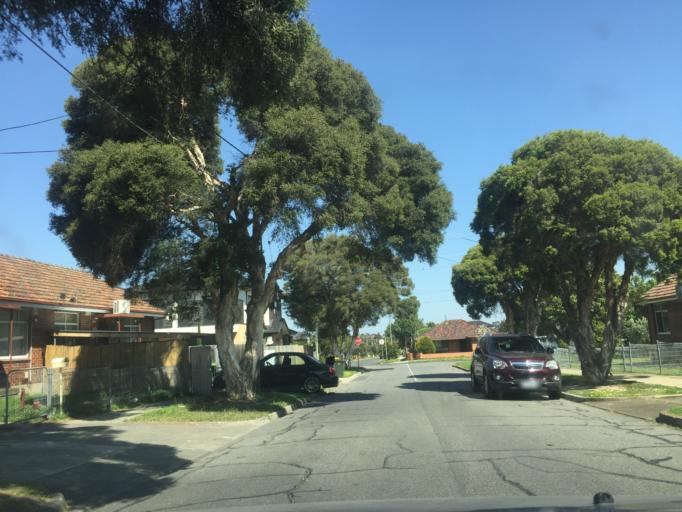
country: AU
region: Victoria
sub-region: Darebin
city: Preston
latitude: -37.7415
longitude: 145.0185
